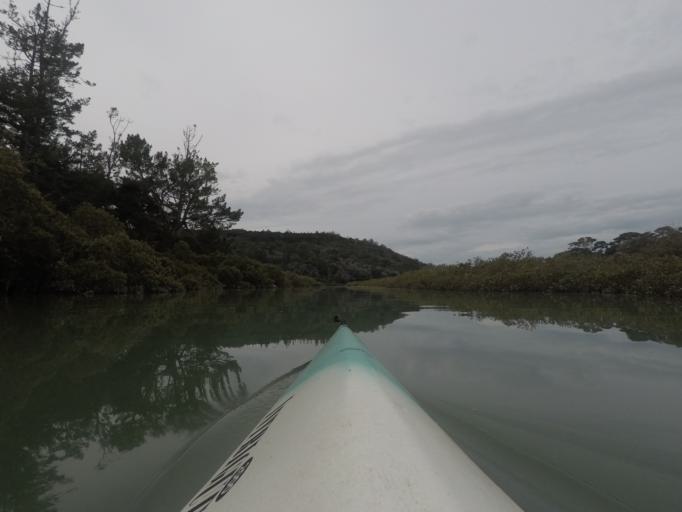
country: NZ
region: Auckland
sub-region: Auckland
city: Rothesay Bay
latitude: -36.6769
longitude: 174.7085
